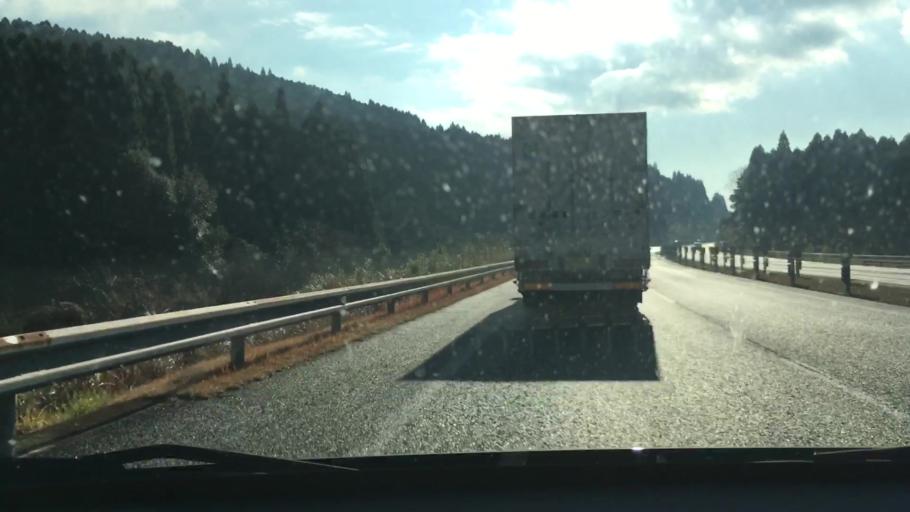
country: JP
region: Kagoshima
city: Okuchi-shinohara
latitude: 31.9607
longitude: 130.7433
